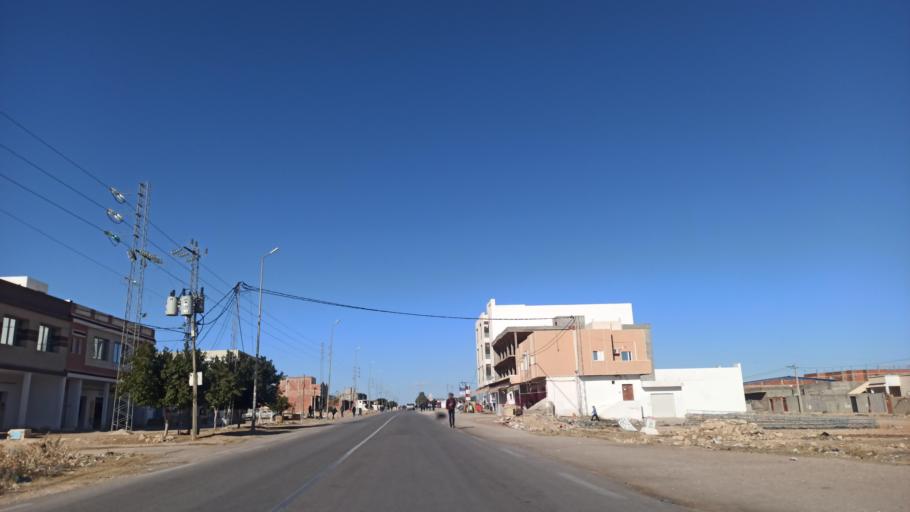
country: TN
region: Sidi Bu Zayd
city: Jilma
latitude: 35.2803
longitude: 9.4189
